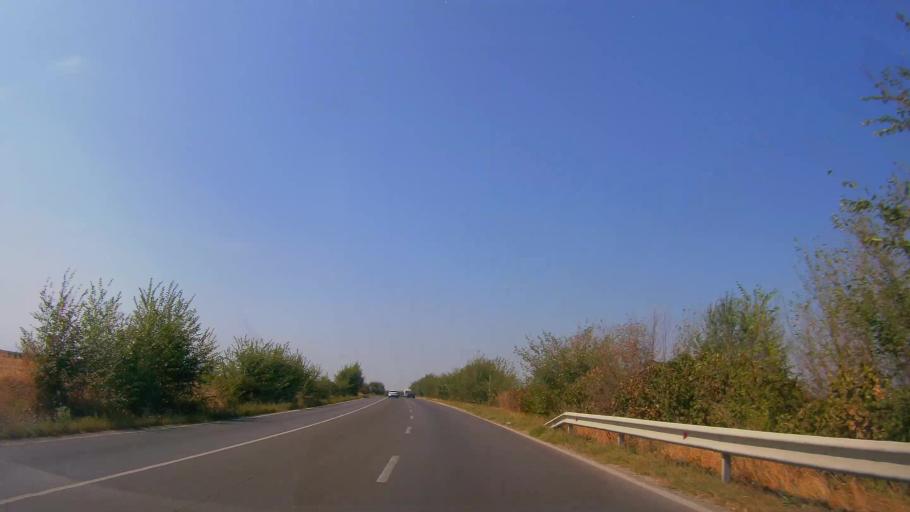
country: BG
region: Ruse
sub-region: Obshtina Vetovo
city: Senovo
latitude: 43.5642
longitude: 26.3394
